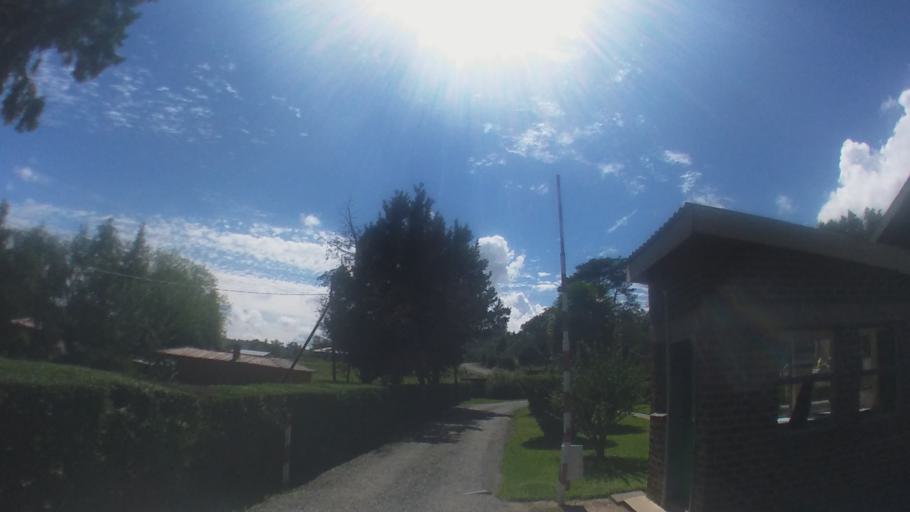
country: LS
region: Maseru
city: Nako
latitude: -29.6252
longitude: 27.5070
